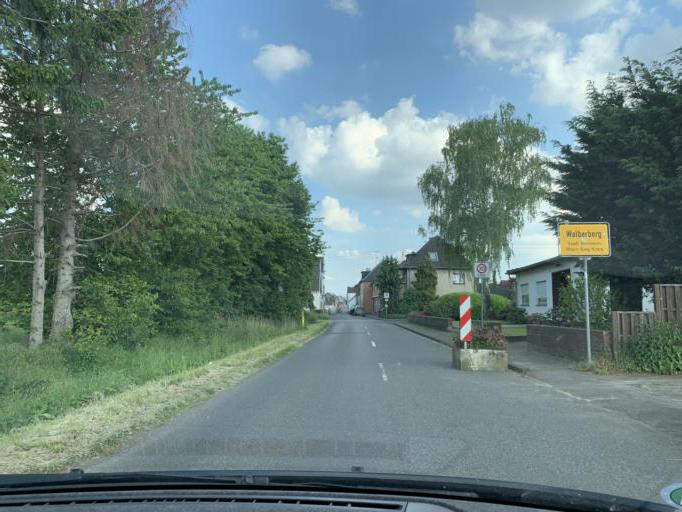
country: DE
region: North Rhine-Westphalia
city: Bruhl
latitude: 50.8002
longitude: 6.9064
